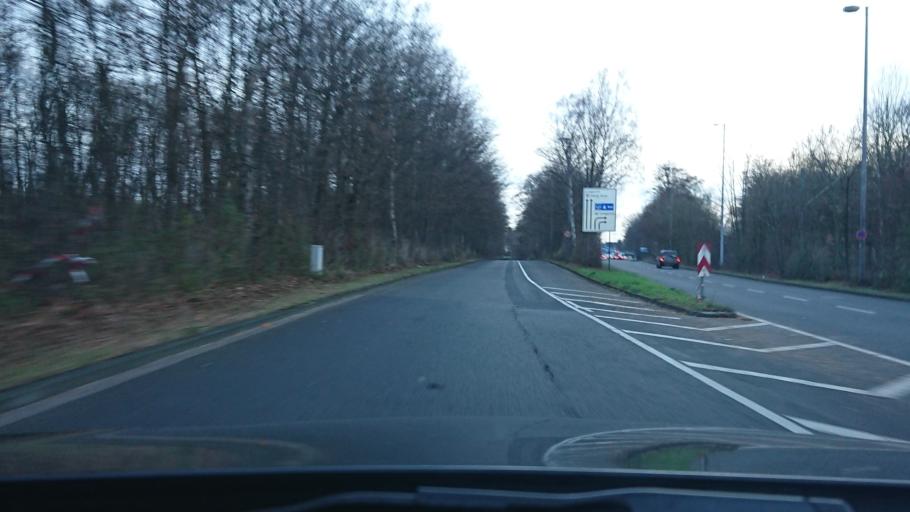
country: DE
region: North Rhine-Westphalia
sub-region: Regierungsbezirk Koln
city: Bilderstoeckchen
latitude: 51.0034
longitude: 6.9132
